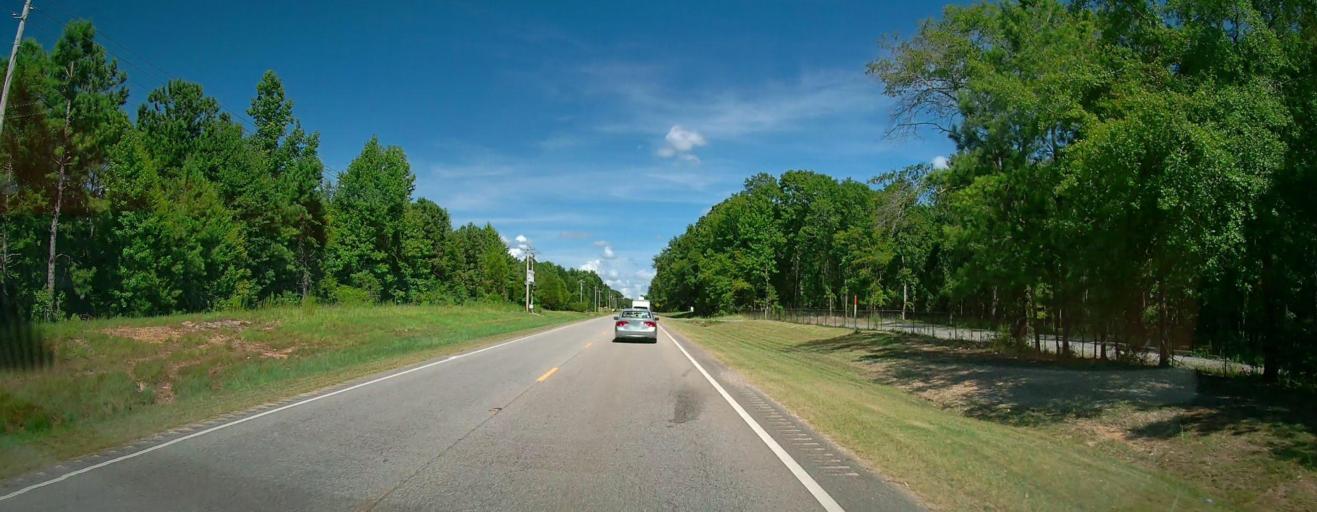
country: US
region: Alabama
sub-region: Elmore County
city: Tallassee
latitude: 32.3988
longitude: -85.9260
